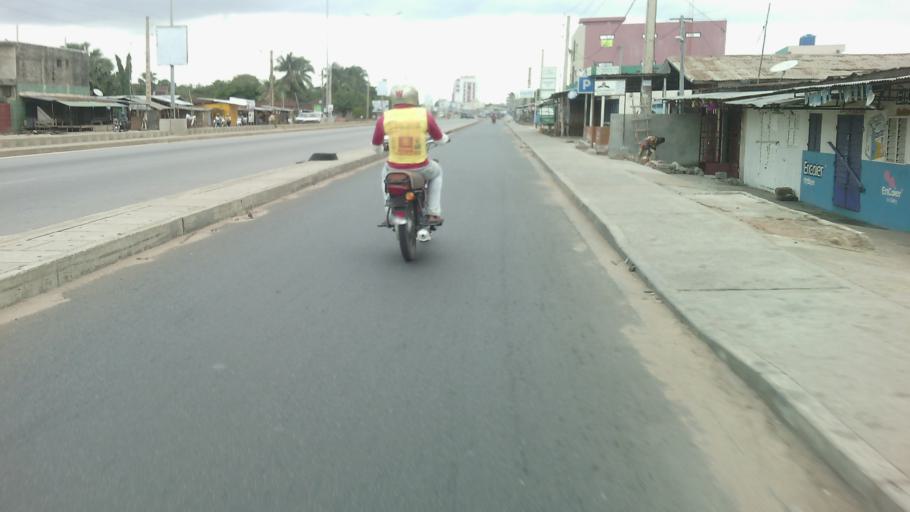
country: BJ
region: Atlantique
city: Abomey-Calavi
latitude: 6.4377
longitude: 2.3526
